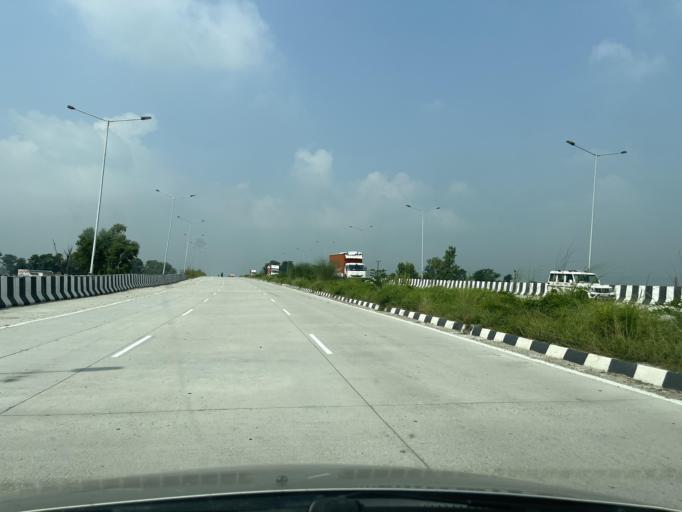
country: IN
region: Uttarakhand
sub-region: Udham Singh Nagar
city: Kashipur
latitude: 29.1664
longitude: 78.9789
